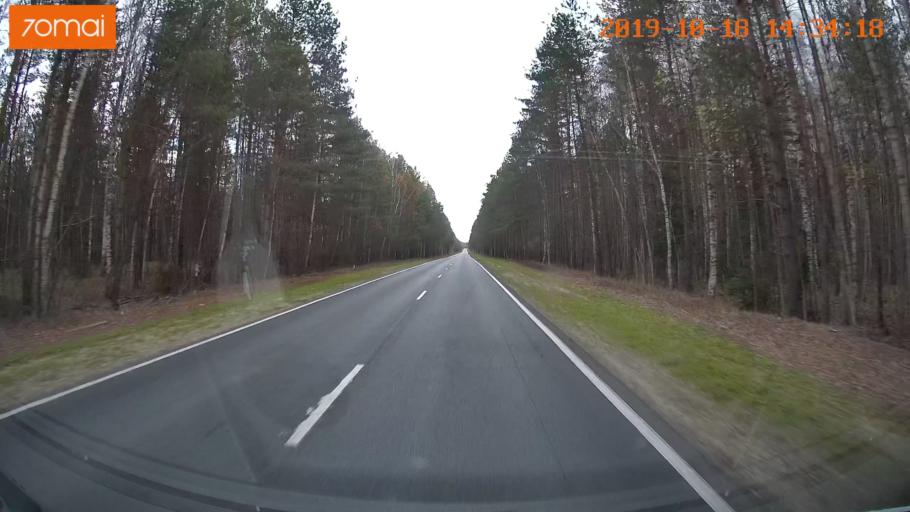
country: RU
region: Vladimir
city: Velikodvorskiy
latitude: 55.2107
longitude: 40.6134
